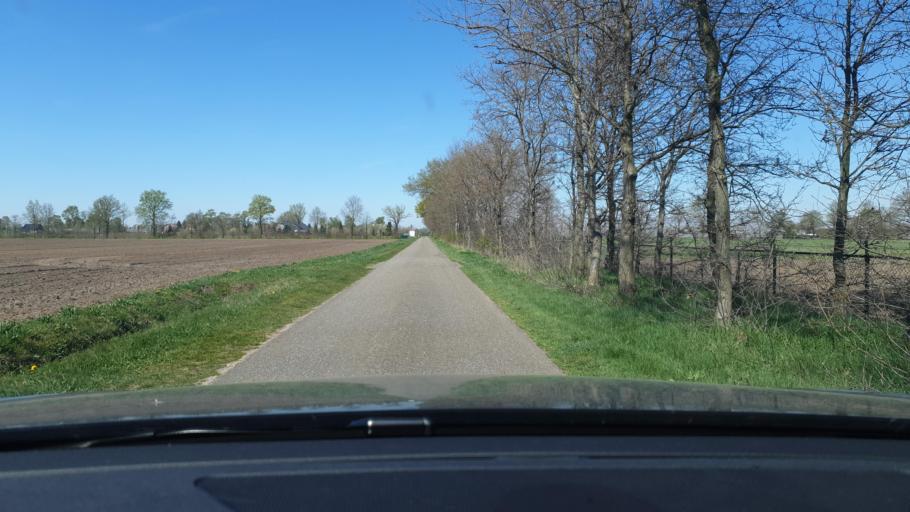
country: NL
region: Limburg
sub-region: Gemeente Venlo
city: Arcen
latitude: 51.4515
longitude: 6.1093
